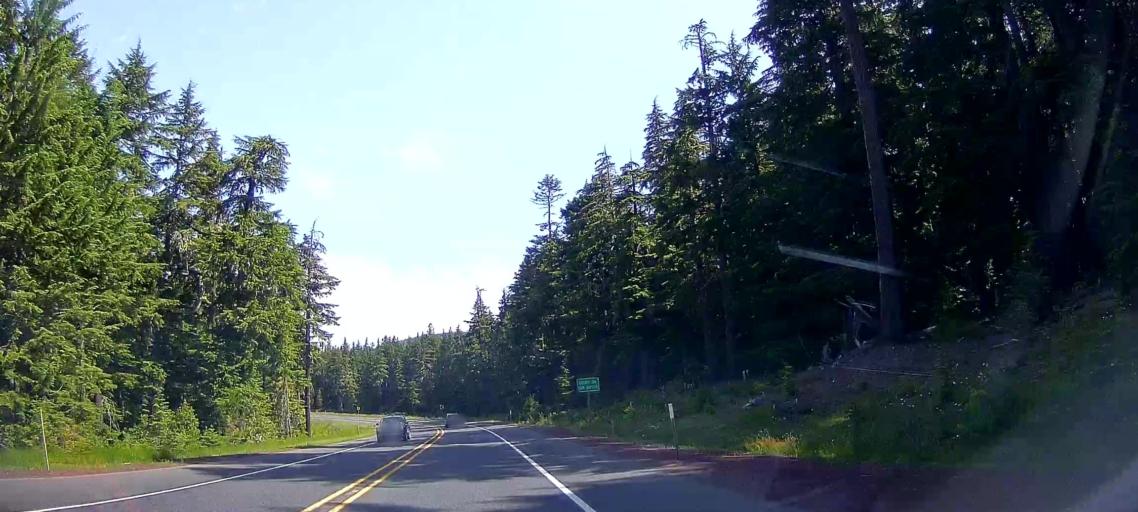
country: US
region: Oregon
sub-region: Clackamas County
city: Mount Hood Village
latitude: 45.1852
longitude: -121.6767
